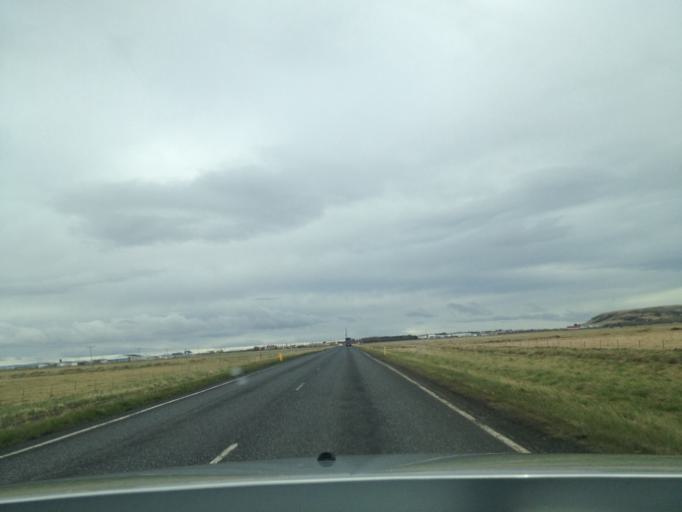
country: IS
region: South
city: Vestmannaeyjar
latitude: 63.7334
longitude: -20.2349
